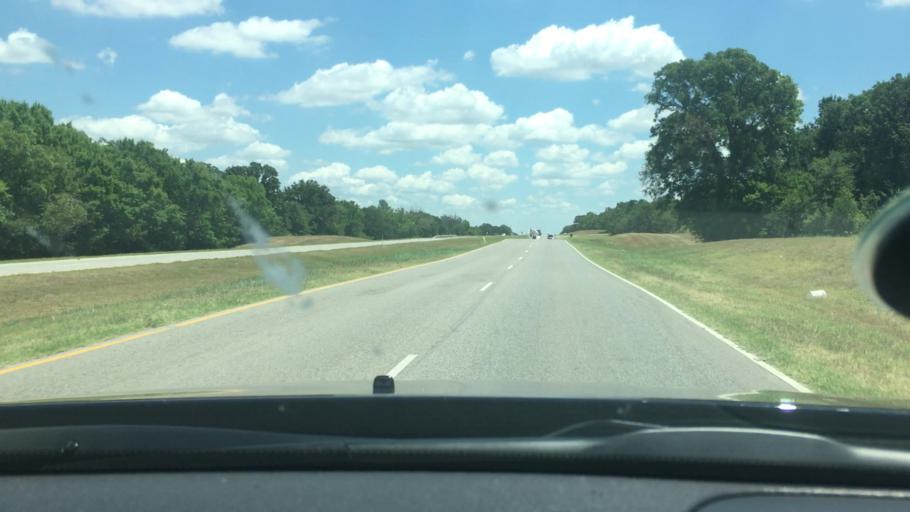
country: US
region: Oklahoma
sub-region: Carter County
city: Wilson
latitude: 34.1728
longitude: -97.3988
